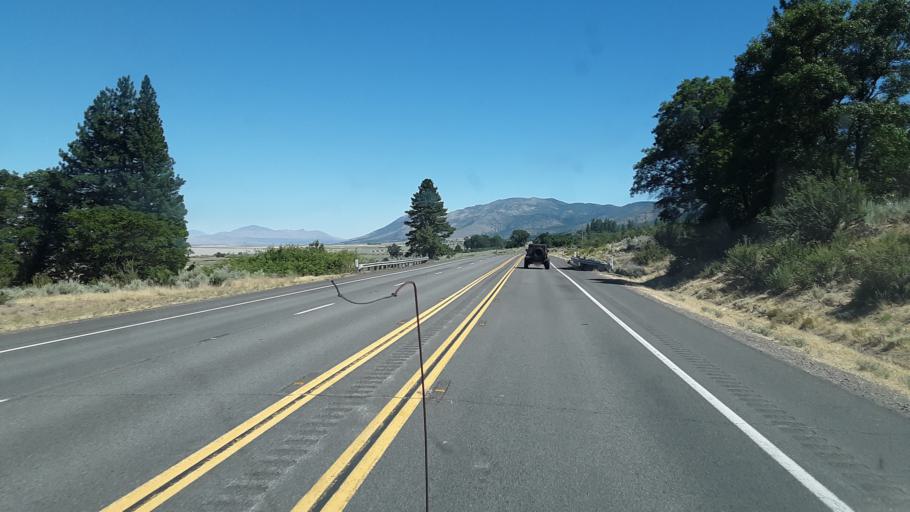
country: US
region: California
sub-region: Lassen County
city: Janesville
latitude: 40.2174
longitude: -120.4284
